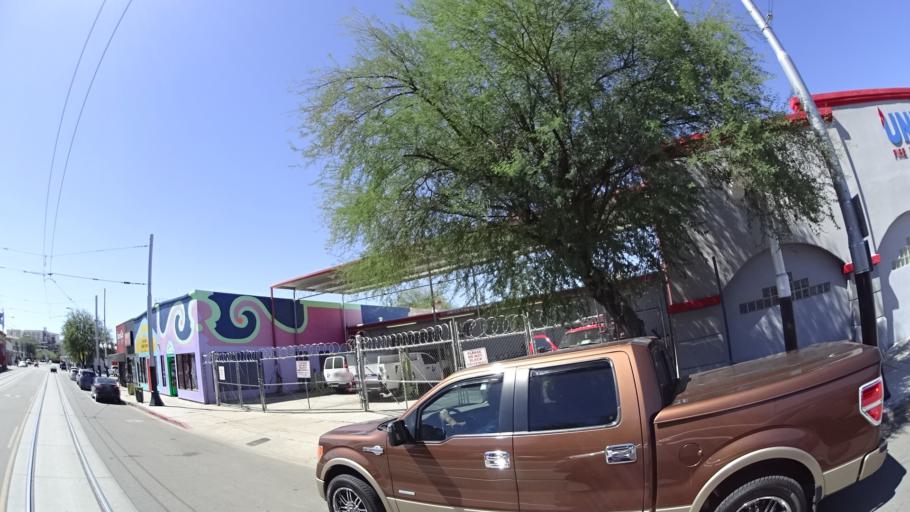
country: US
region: Arizona
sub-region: Pima County
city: South Tucson
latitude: 32.2261
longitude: -110.9656
